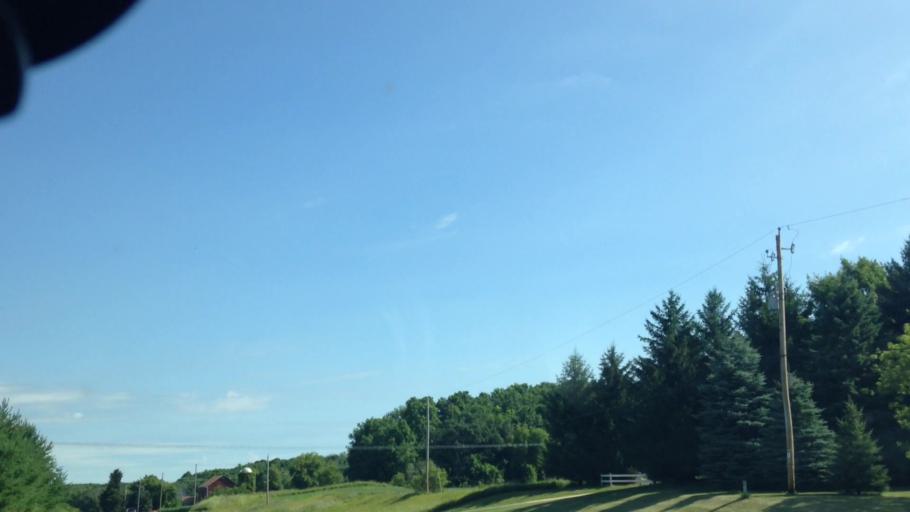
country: US
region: Wisconsin
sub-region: Washington County
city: Slinger
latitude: 43.3551
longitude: -88.2611
